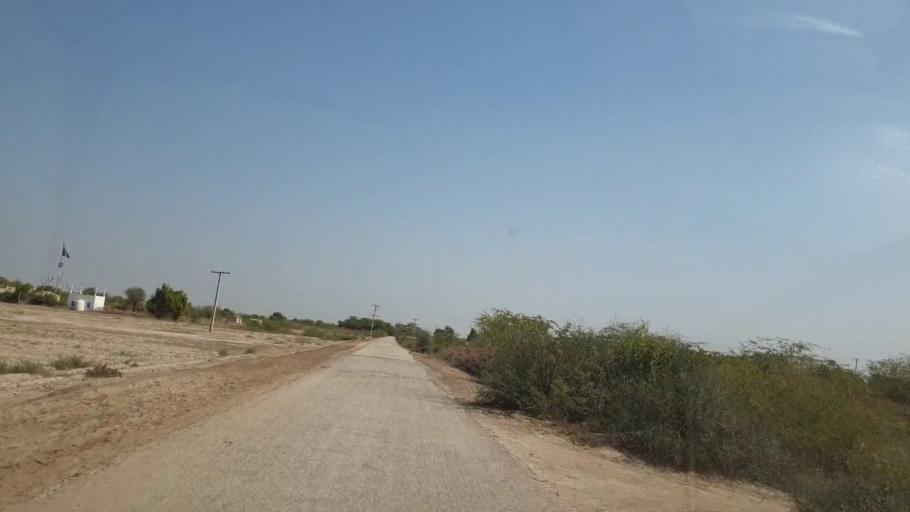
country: PK
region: Sindh
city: Kunri
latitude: 25.0905
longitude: 69.5213
